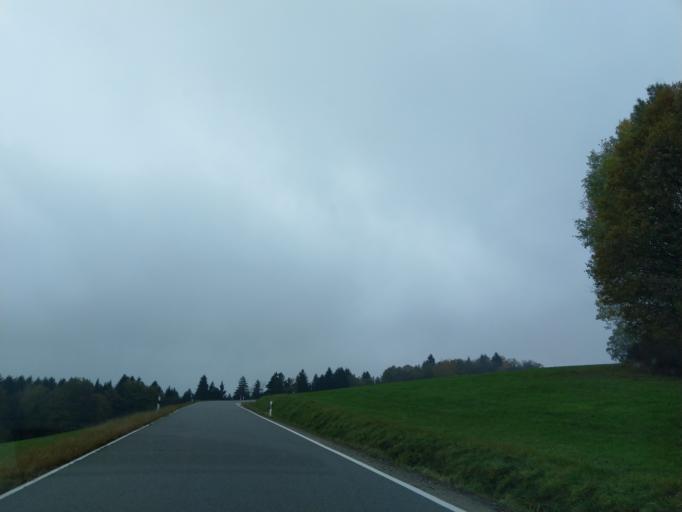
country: DE
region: Bavaria
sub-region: Lower Bavaria
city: Auerbach
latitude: 48.7886
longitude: 13.1117
